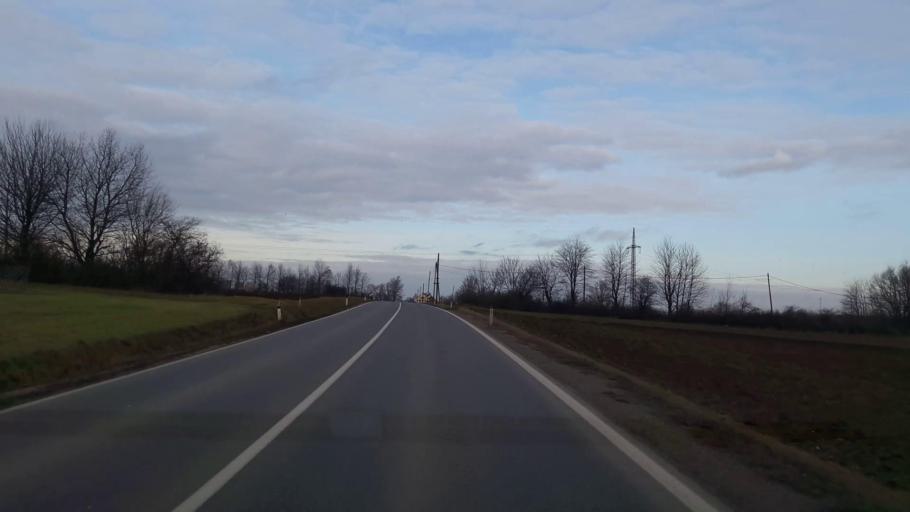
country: AT
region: Lower Austria
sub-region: Politischer Bezirk Mistelbach
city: Staatz
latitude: 48.6359
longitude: 16.5176
